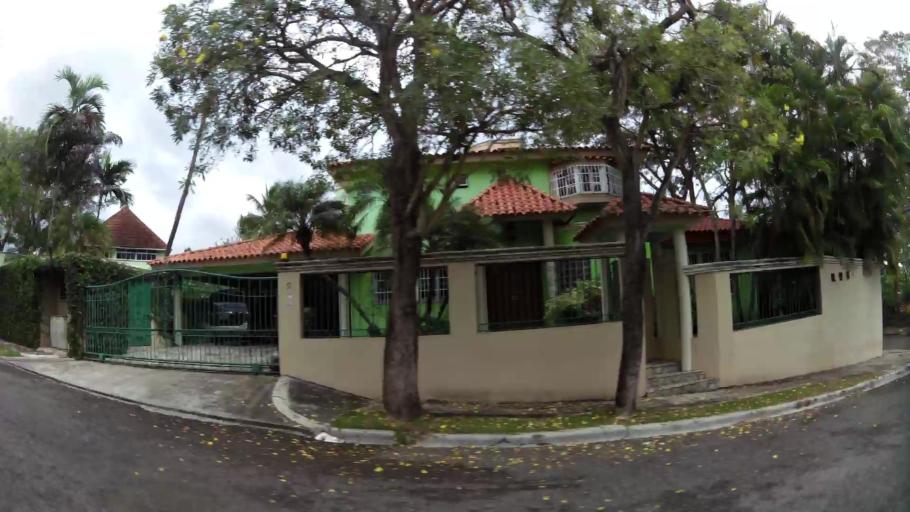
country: DO
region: Nacional
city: Santo Domingo
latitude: 18.5054
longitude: -69.9701
